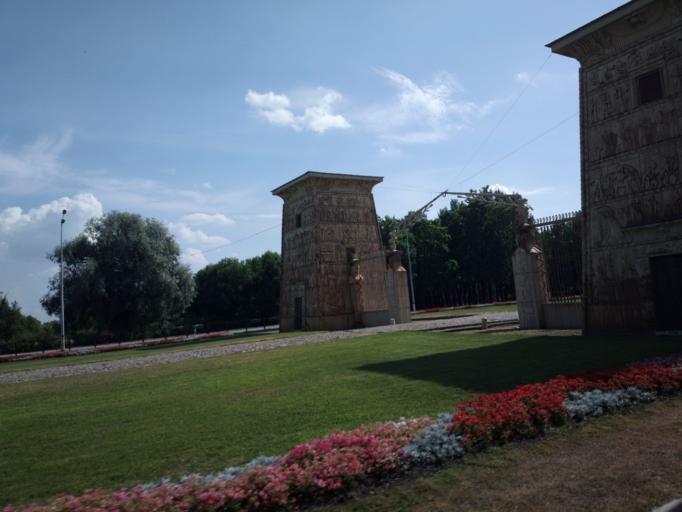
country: RU
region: St.-Petersburg
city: Pushkin
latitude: 59.7295
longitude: 30.3941
